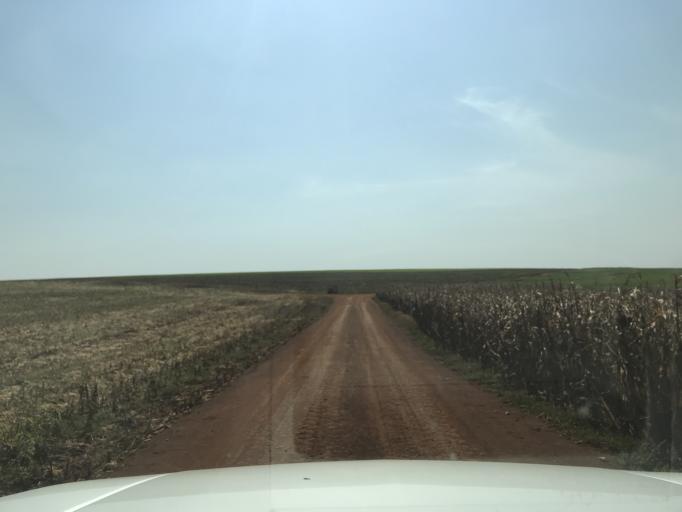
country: BR
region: Parana
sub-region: Palotina
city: Palotina
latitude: -24.2311
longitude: -53.7448
